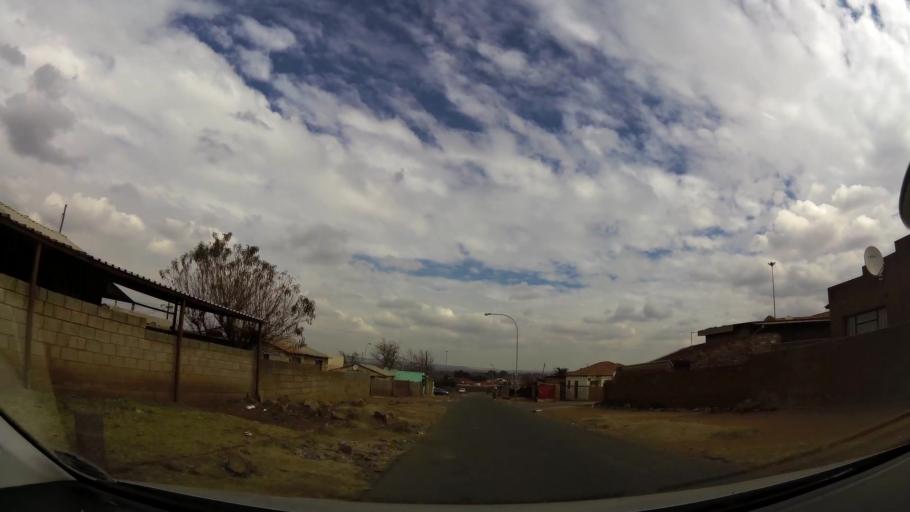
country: ZA
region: Gauteng
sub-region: City of Johannesburg Metropolitan Municipality
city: Soweto
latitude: -26.2785
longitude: 27.8499
